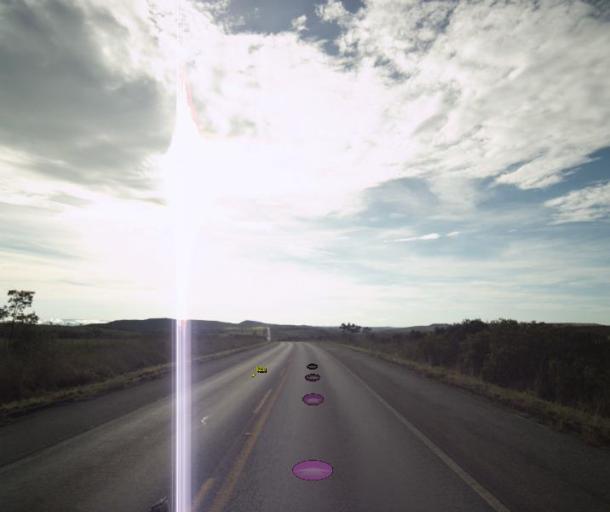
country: BR
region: Goias
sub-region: Pirenopolis
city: Pirenopolis
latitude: -15.7511
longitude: -48.6413
